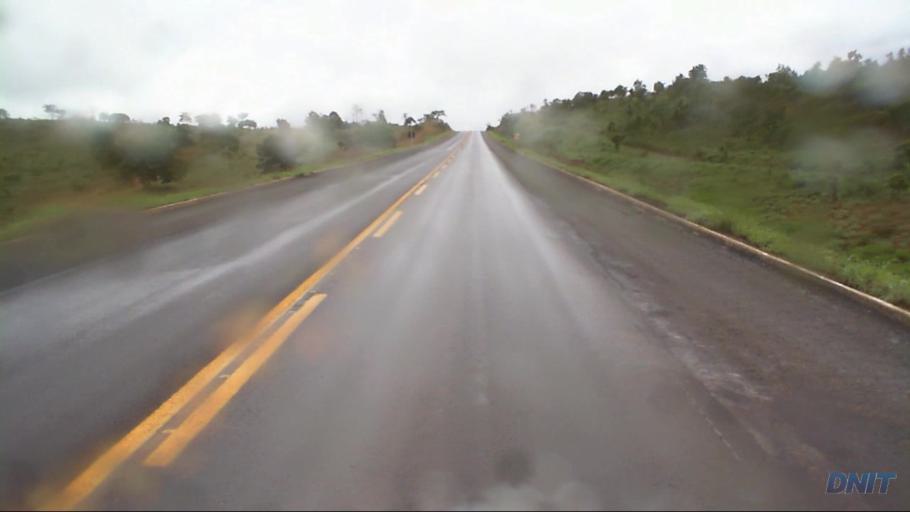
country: BR
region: Goias
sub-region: Padre Bernardo
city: Padre Bernardo
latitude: -15.2014
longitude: -48.4546
